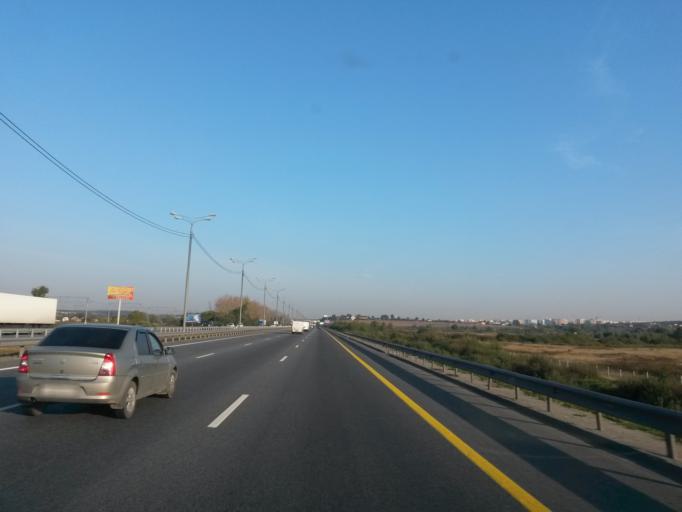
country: RU
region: Moskovskaya
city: Yam
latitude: 55.5019
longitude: 37.7261
